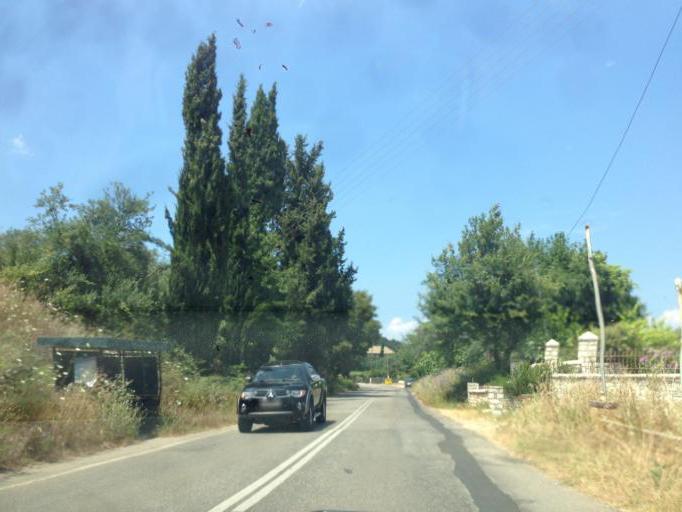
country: GR
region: Ionian Islands
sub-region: Nomos Kerkyras
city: Acharavi
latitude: 39.7807
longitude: 19.9247
